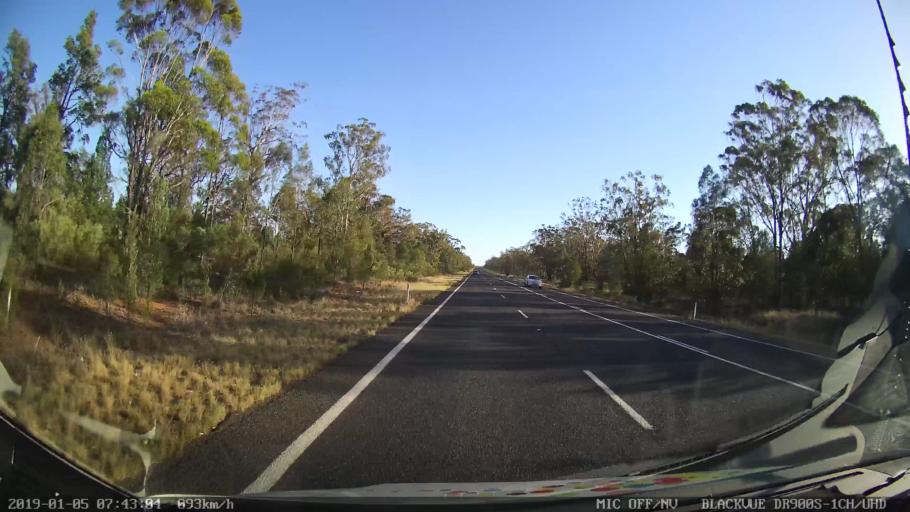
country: AU
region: New South Wales
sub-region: Gilgandra
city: Gilgandra
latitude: -31.8897
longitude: 148.6314
